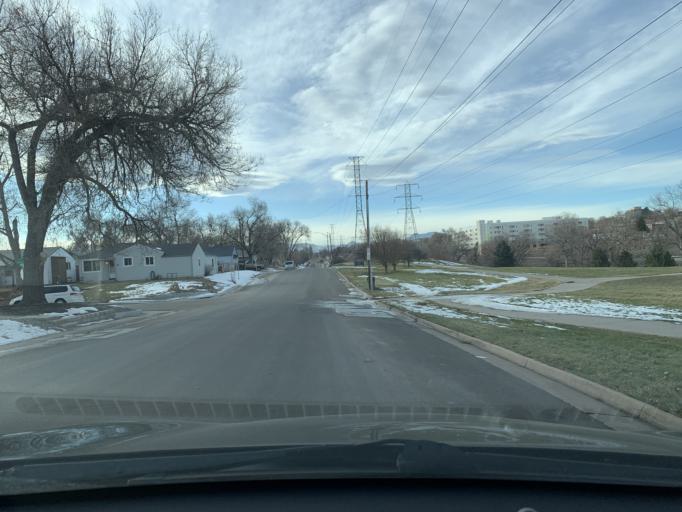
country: US
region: Colorado
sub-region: Jefferson County
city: Edgewater
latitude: 39.7348
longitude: -105.0282
